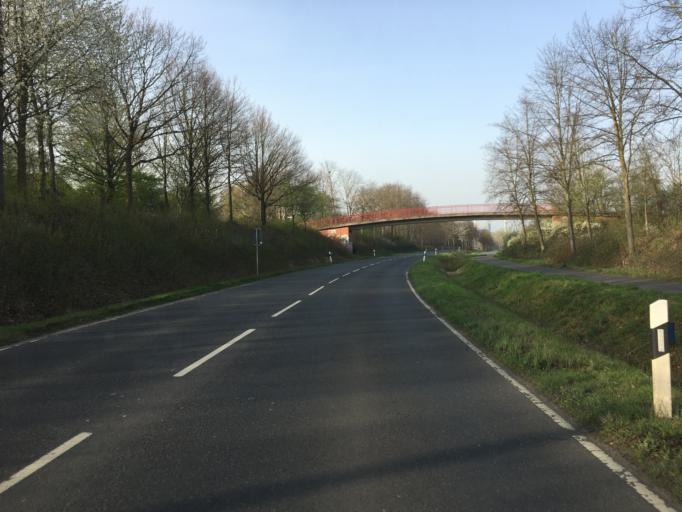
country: DE
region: North Rhine-Westphalia
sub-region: Regierungsbezirk Koln
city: Hurth
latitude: 50.8732
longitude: 6.8645
